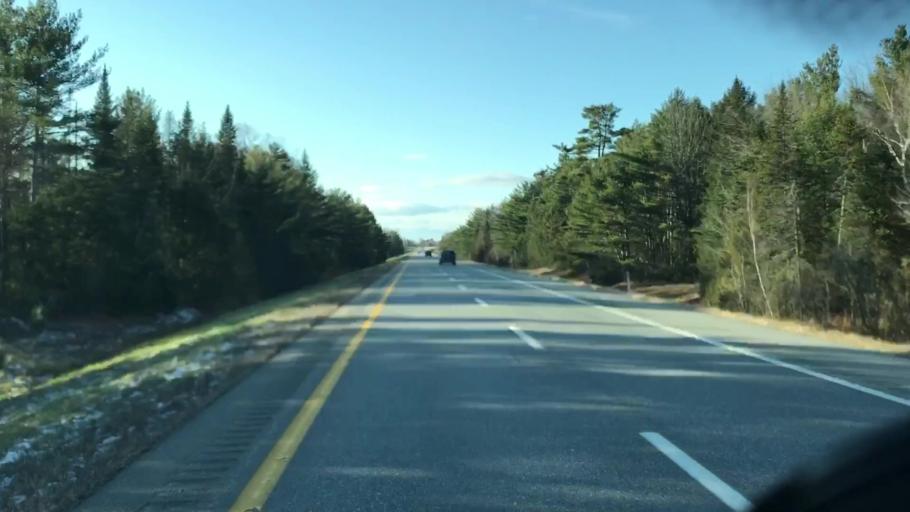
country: US
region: Maine
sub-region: Penobscot County
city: Newport
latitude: 44.8120
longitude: -69.2403
